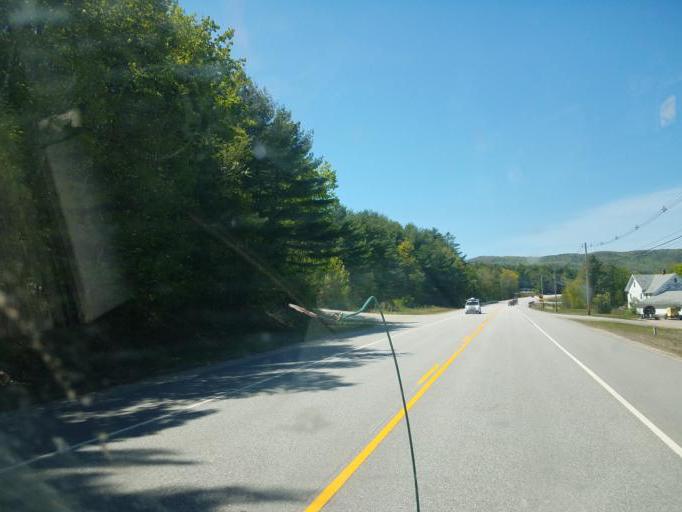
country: US
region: New Hampshire
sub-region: Grafton County
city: Rumney
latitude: 43.7883
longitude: -71.7941
